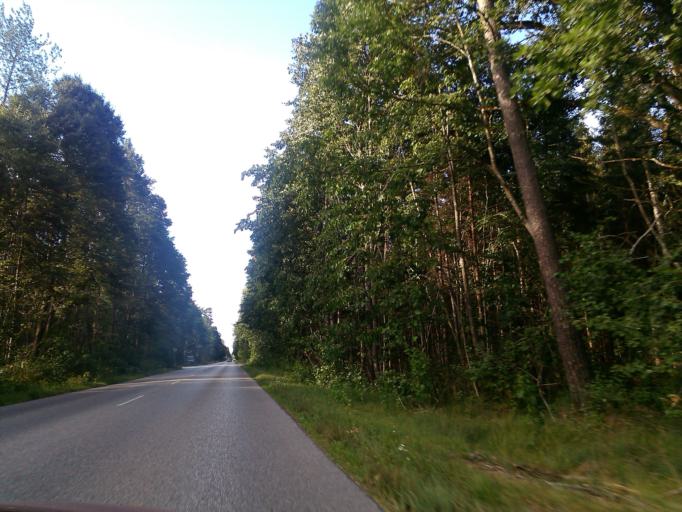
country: DE
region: Bavaria
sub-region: Upper Bavaria
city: Krailling
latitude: 48.1016
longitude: 11.3742
